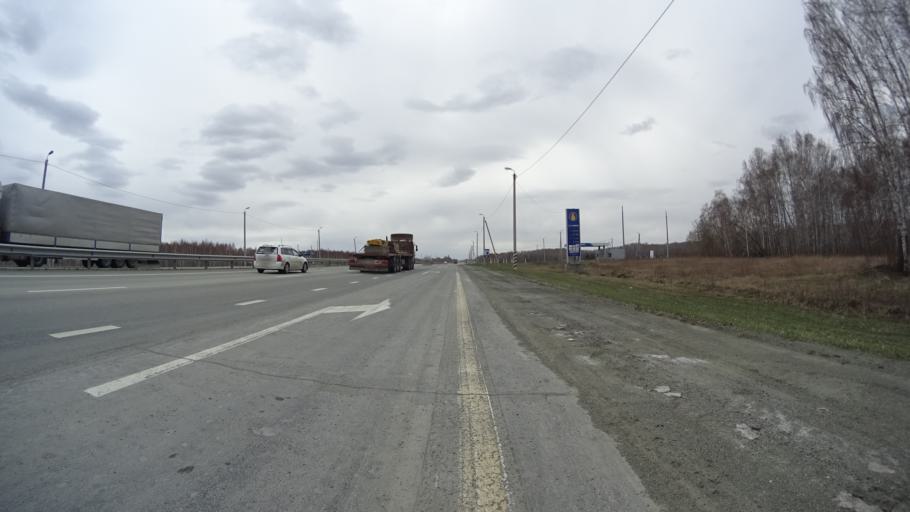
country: RU
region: Chelyabinsk
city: Yemanzhelinka
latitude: 54.8351
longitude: 61.3125
